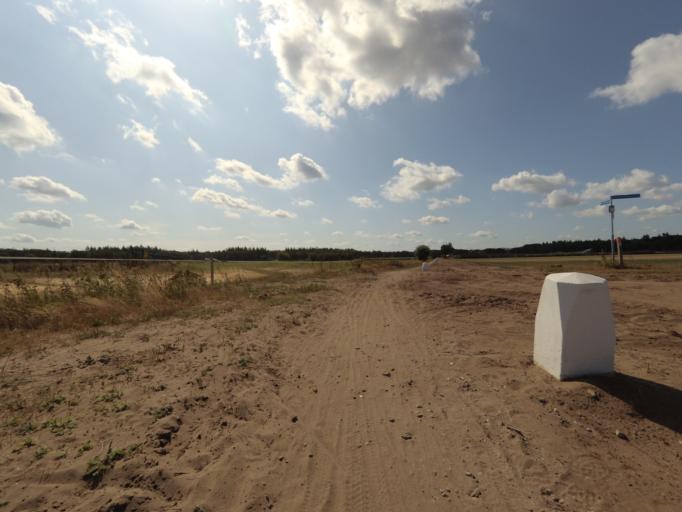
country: NL
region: Overijssel
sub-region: Gemeente Enschede
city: Enschede
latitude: 52.2683
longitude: 6.8684
